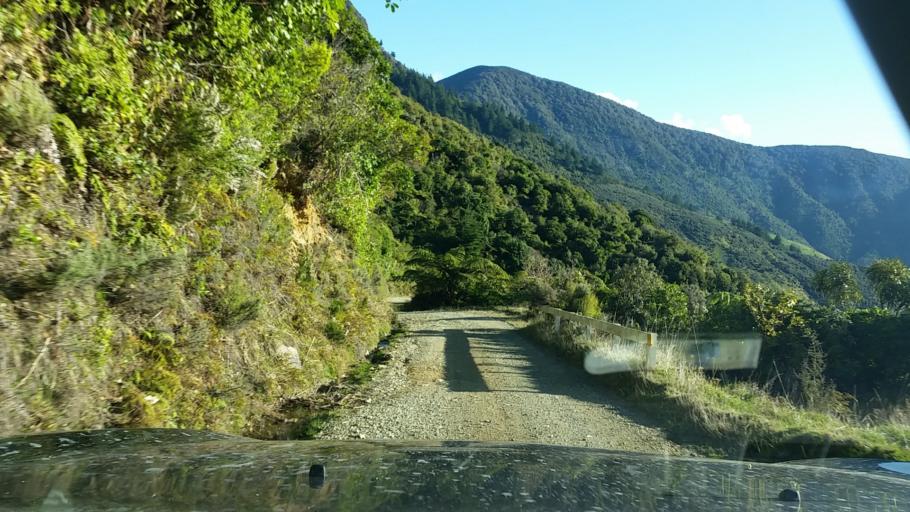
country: NZ
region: Marlborough
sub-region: Marlborough District
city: Picton
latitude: -41.0229
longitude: 174.1583
